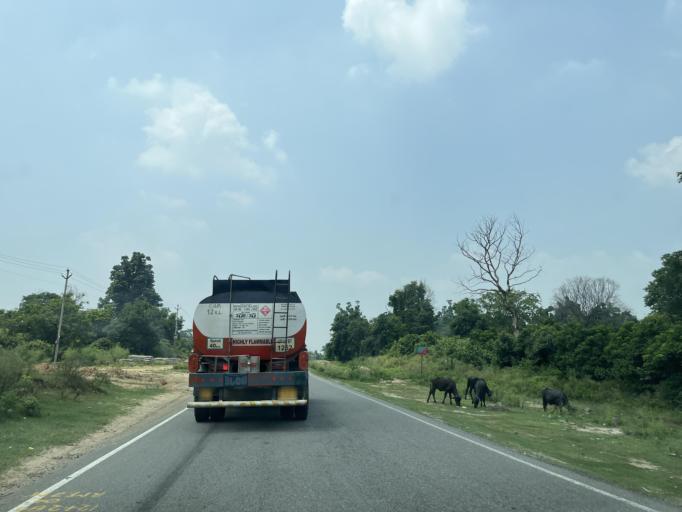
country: IN
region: Uttarakhand
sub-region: Haridwar
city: Haridwar
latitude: 29.8440
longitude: 78.1888
